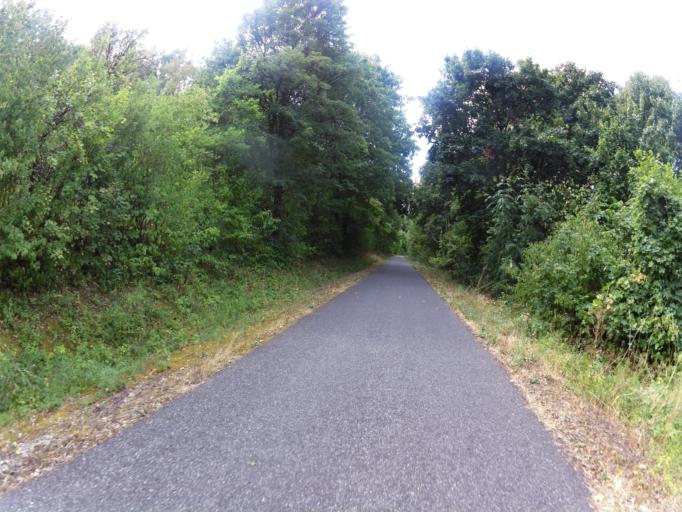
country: DE
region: Bavaria
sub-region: Regierungsbezirk Unterfranken
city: Ochsenfurt
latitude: 49.6643
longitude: 10.0422
